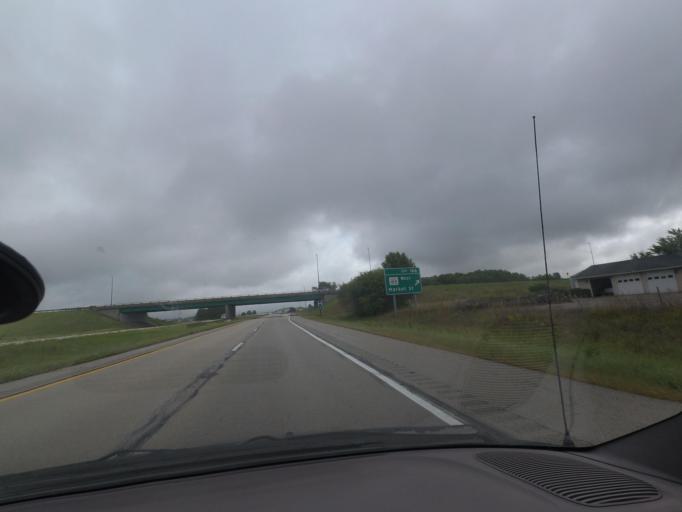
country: US
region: Illinois
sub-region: Piatt County
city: Monticello
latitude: 40.0527
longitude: -88.5677
